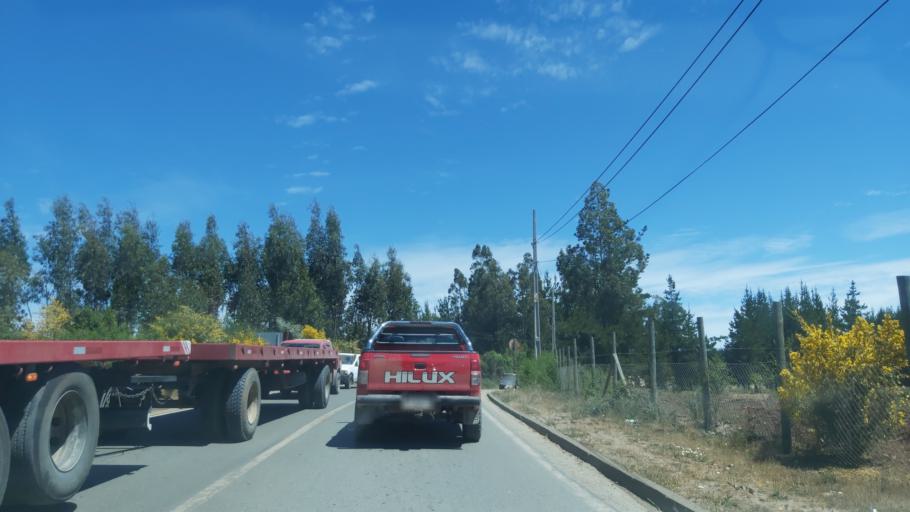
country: CL
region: Maule
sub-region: Provincia de Talca
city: Constitucion
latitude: -35.3898
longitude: -72.4240
